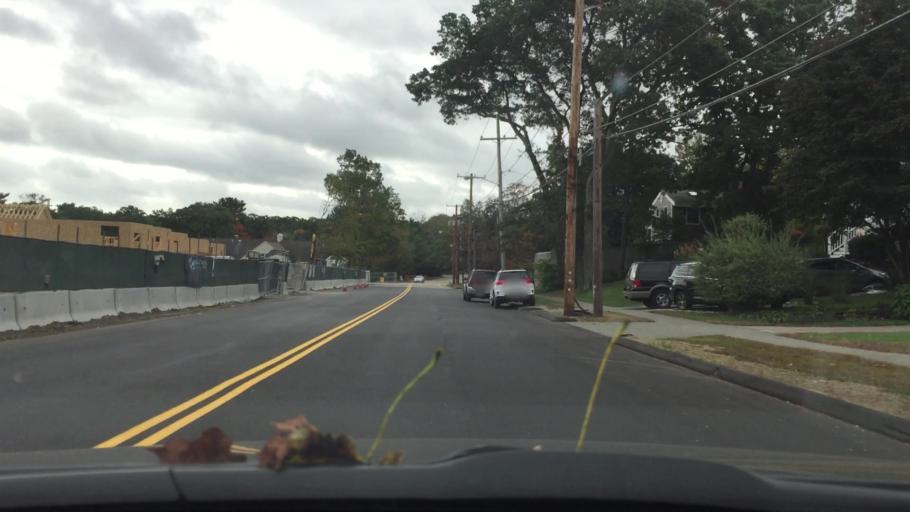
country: US
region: Massachusetts
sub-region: Norfolk County
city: Needham
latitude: 42.2844
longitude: -71.2084
